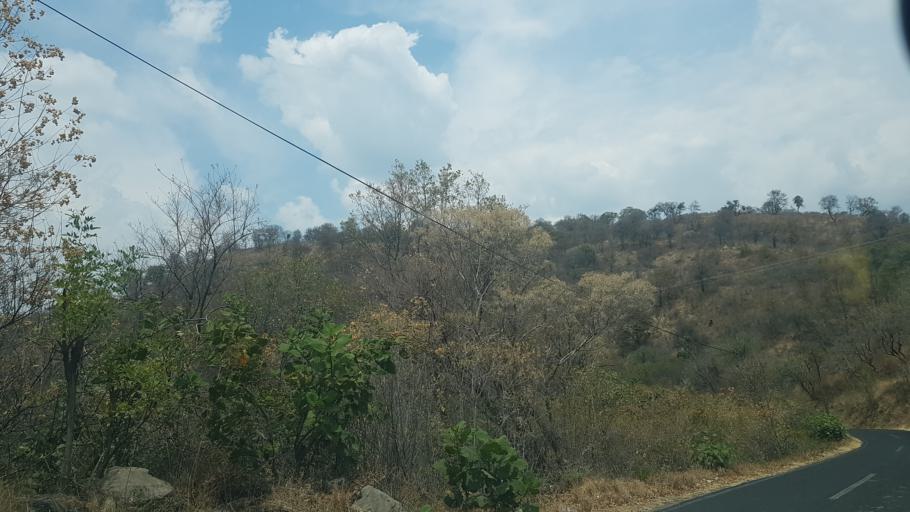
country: MX
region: Puebla
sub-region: Tochimilco
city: La Magdalena Yancuitlalpan
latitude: 18.8760
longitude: -98.5993
